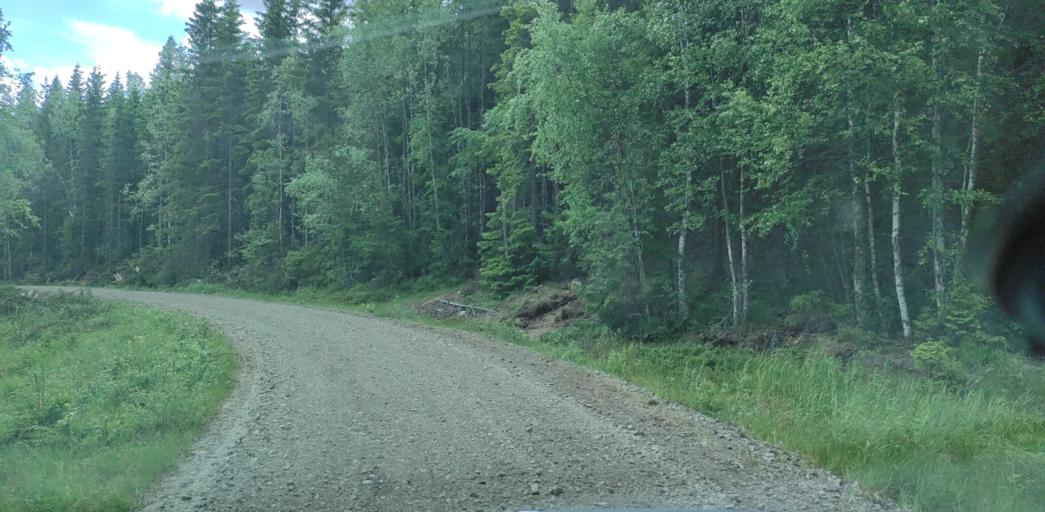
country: SE
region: Vaermland
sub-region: Munkfors Kommun
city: Munkfors
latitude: 59.9704
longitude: 13.4077
